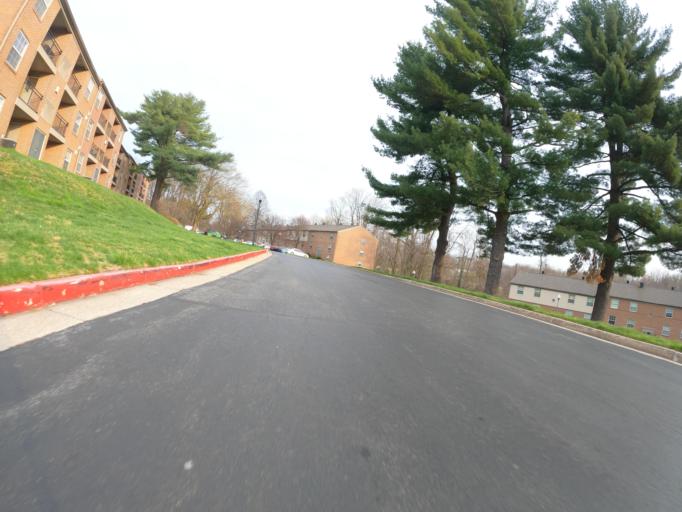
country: US
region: Maryland
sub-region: Howard County
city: Ellicott City
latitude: 39.2903
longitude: -76.8166
